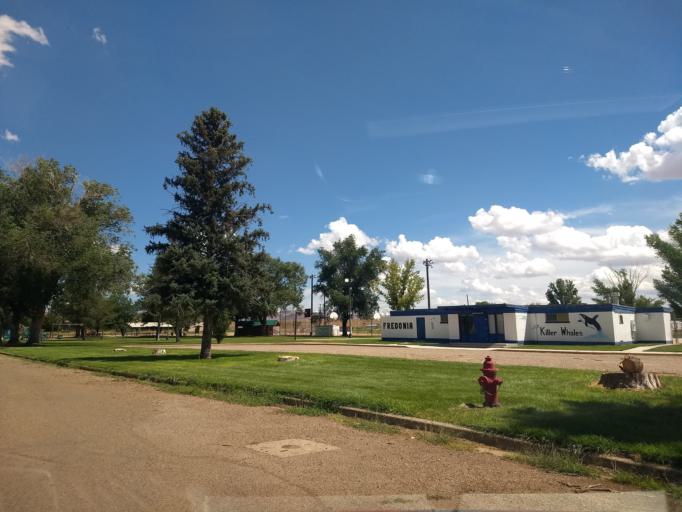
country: US
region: Arizona
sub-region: Coconino County
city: Fredonia
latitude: 36.9491
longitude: -112.5221
